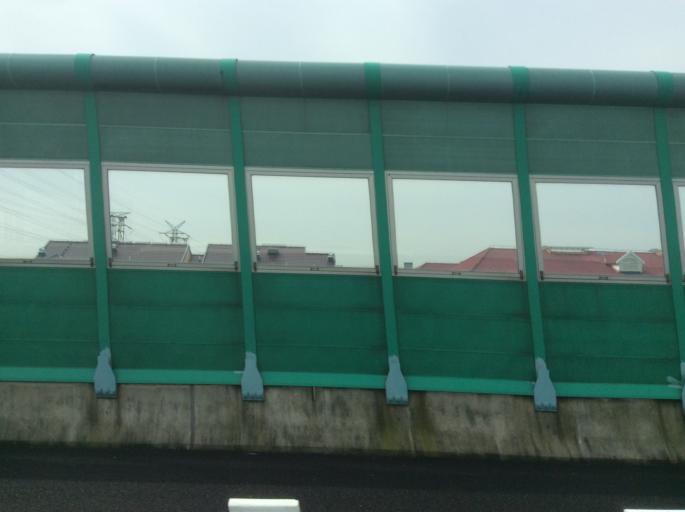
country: CN
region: Shanghai Shi
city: Kangqiao
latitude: 31.1979
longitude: 121.6656
